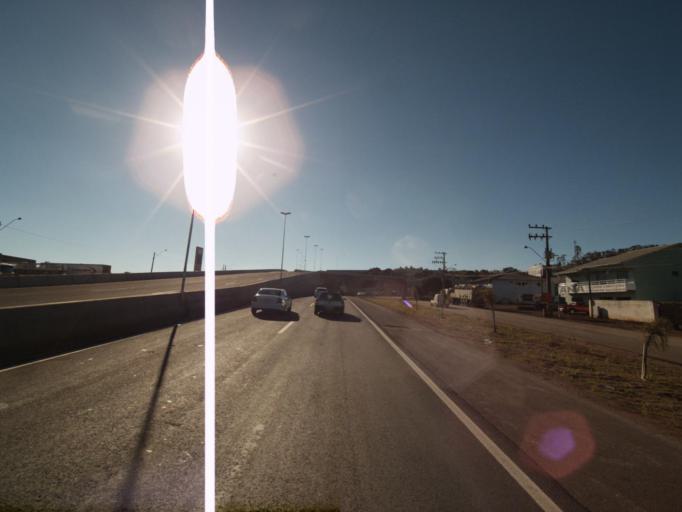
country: BR
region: Santa Catarina
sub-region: Chapeco
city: Chapeco
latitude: -27.0008
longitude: -52.6454
